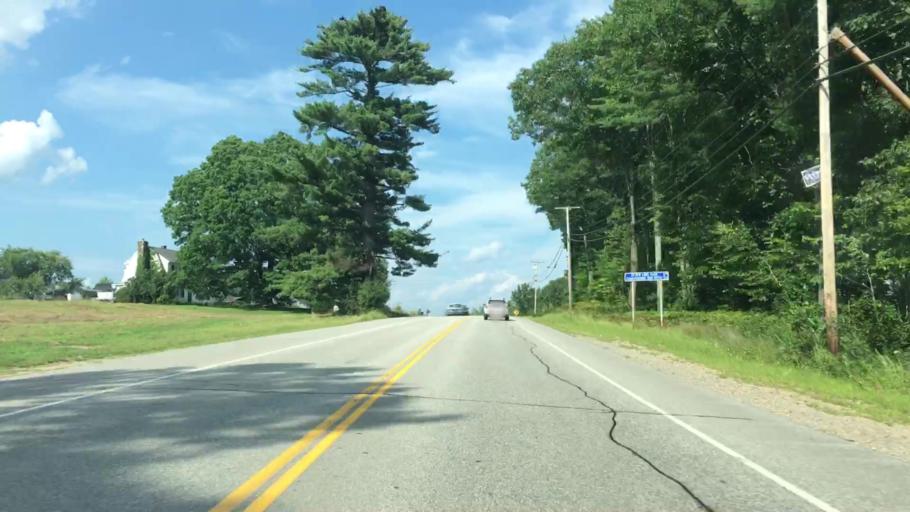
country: US
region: New Hampshire
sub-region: Belknap County
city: Sanbornton
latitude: 43.4699
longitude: -71.5453
